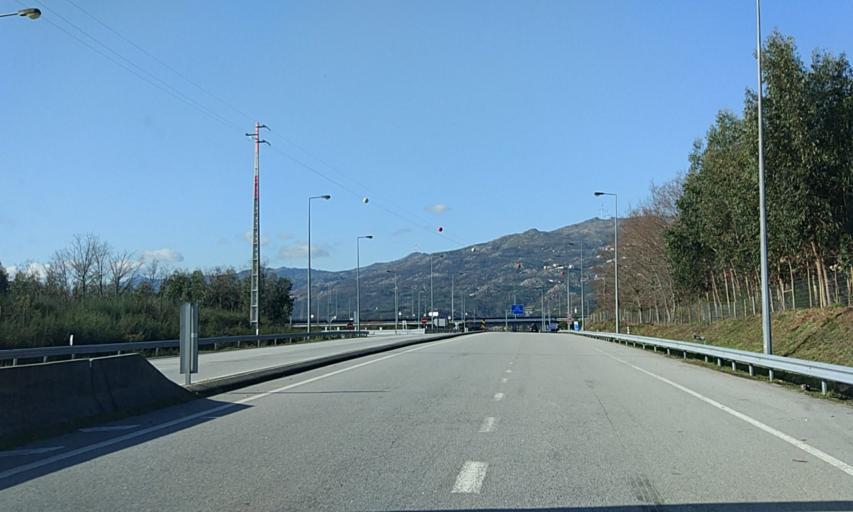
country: PT
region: Viseu
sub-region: Vouzela
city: Vouzela
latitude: 40.6482
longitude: -8.0573
